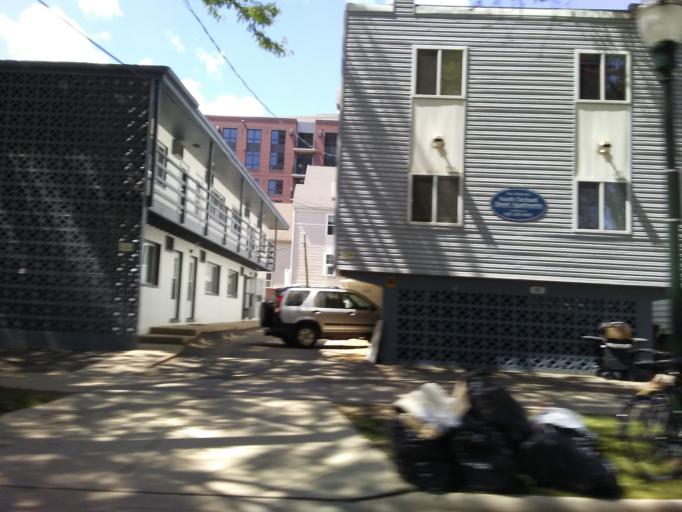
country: US
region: Wisconsin
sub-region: Dane County
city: Madison
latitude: 43.0708
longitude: -89.4074
